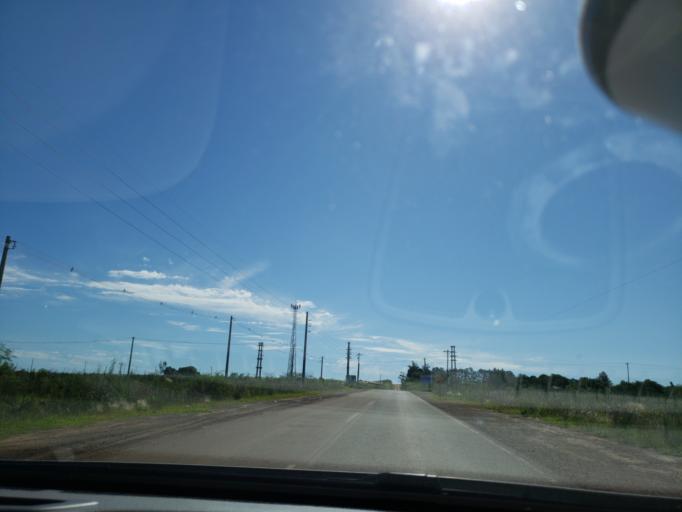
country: PY
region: Itapua
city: San Juan del Parana
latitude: -27.3908
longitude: -55.9893
